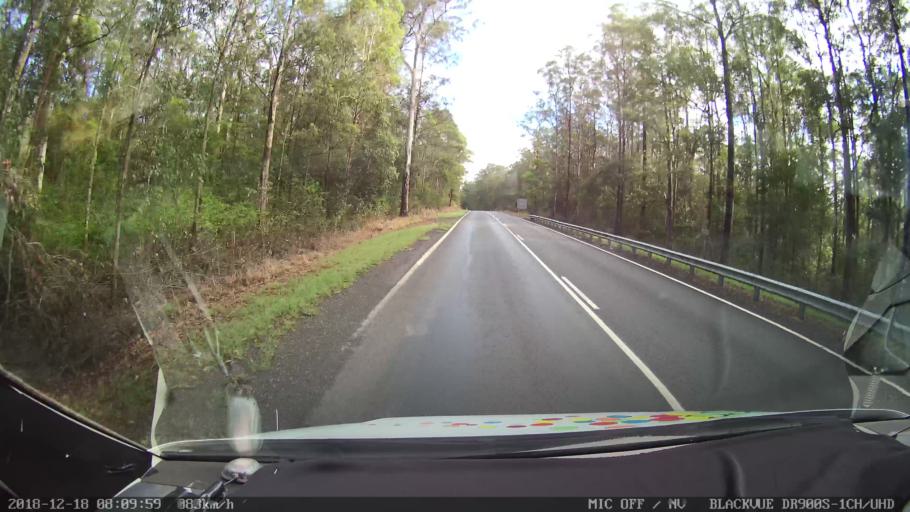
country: AU
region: New South Wales
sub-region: Kyogle
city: Kyogle
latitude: -28.3667
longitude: 152.6594
